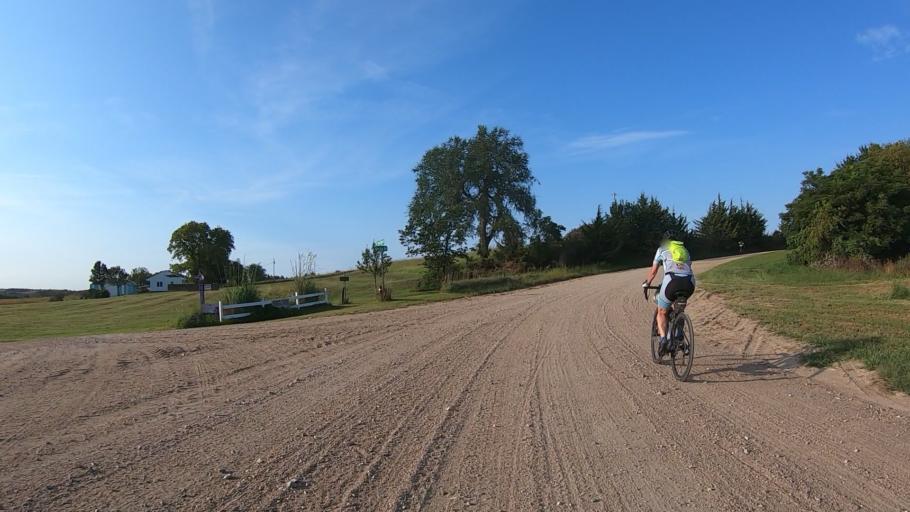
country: US
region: Kansas
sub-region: Marshall County
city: Blue Rapids
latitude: 39.6757
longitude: -96.7840
